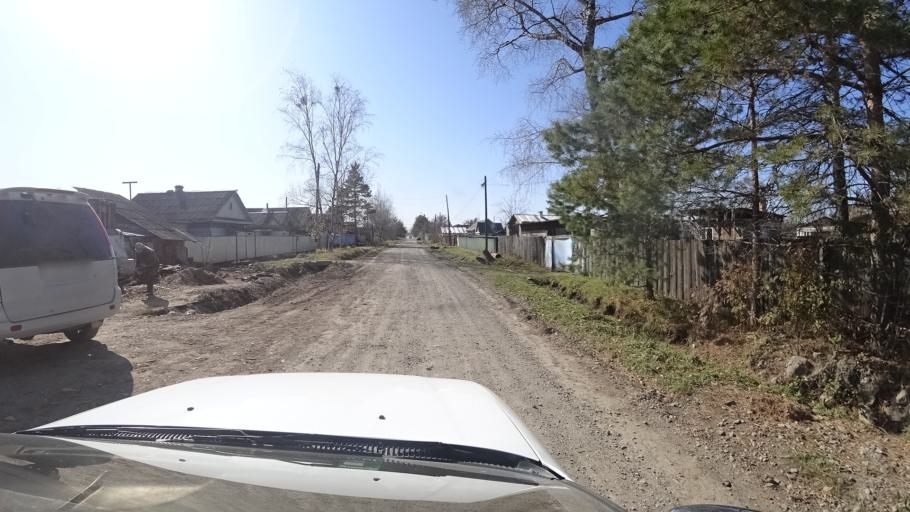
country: RU
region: Primorskiy
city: Dal'nerechensk
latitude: 45.9301
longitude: 133.7523
